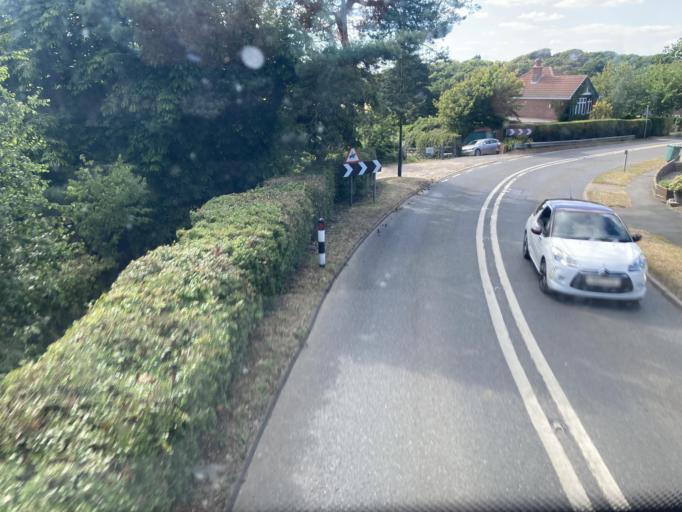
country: GB
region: England
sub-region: Isle of Wight
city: Shanklin
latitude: 50.6280
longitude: -1.1965
